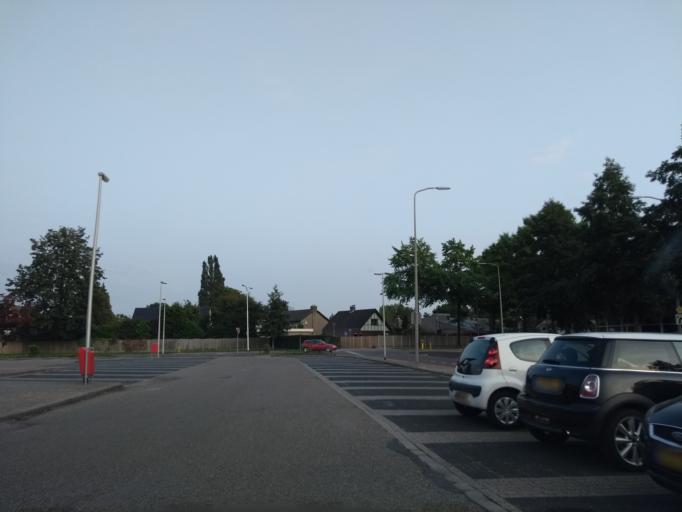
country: NL
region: Overijssel
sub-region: Gemeente Almelo
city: Almelo
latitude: 52.3784
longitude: 6.6779
